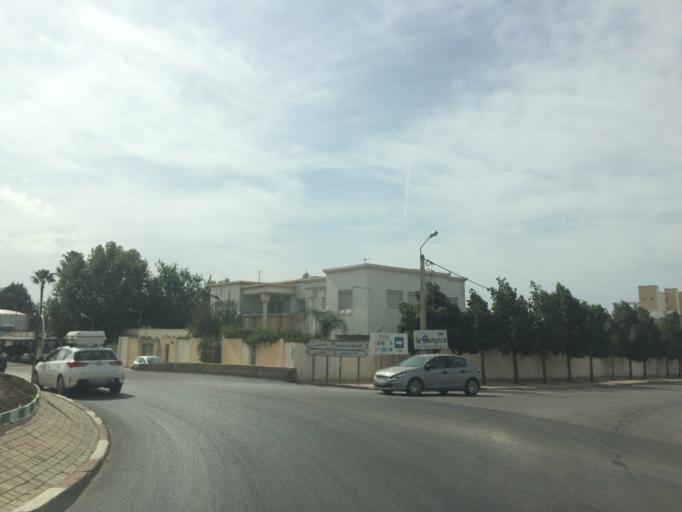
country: MA
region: Meknes-Tafilalet
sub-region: Meknes
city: Meknes
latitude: 33.8271
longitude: -5.5152
